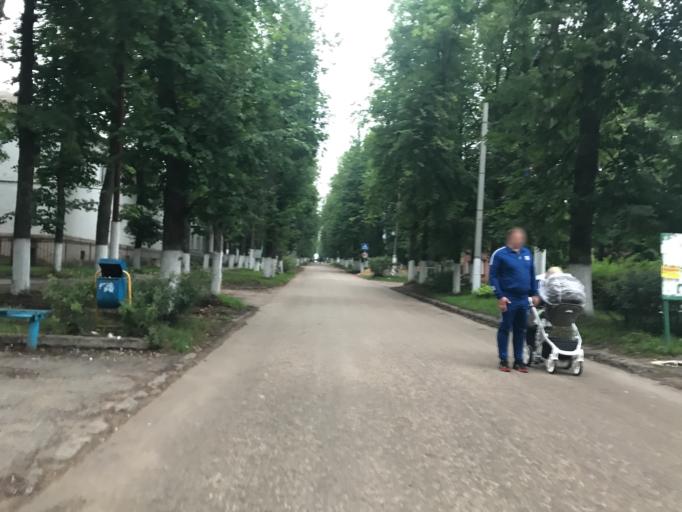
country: RU
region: Tula
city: Priupskiy
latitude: 53.9419
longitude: 37.7015
